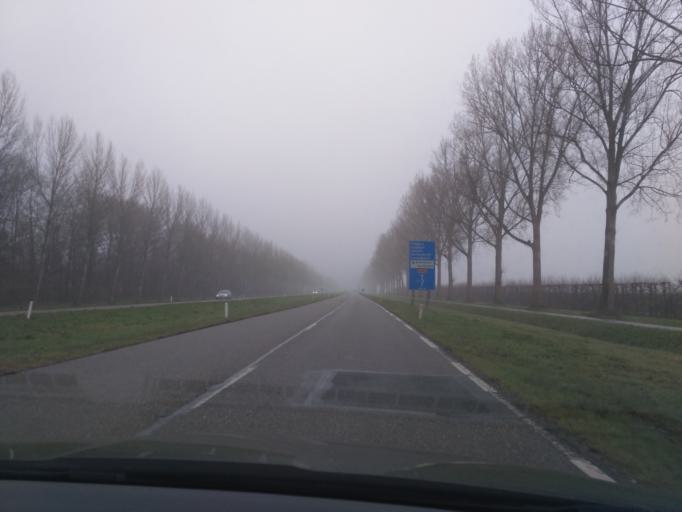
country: NL
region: Flevoland
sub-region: Gemeente Dronten
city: Dronten
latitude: 52.5177
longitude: 5.7334
